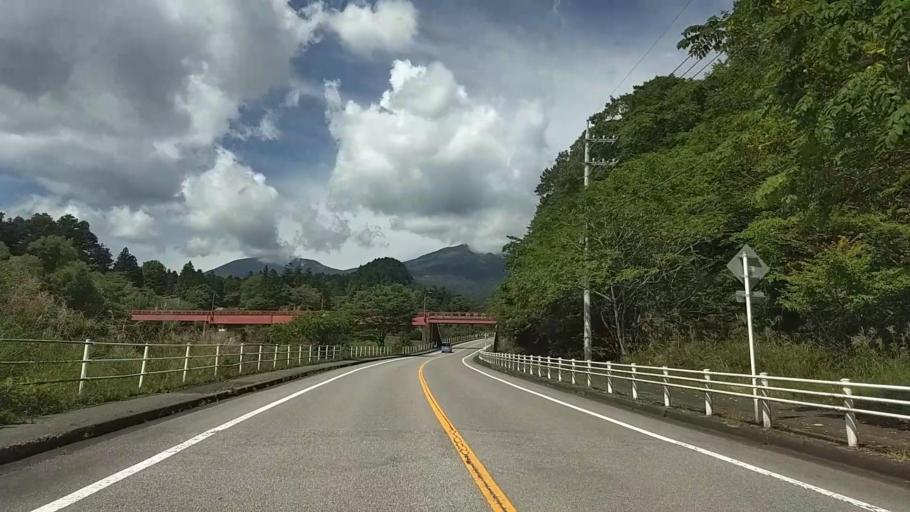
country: JP
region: Tochigi
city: Nikko
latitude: 36.7541
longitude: 139.6082
